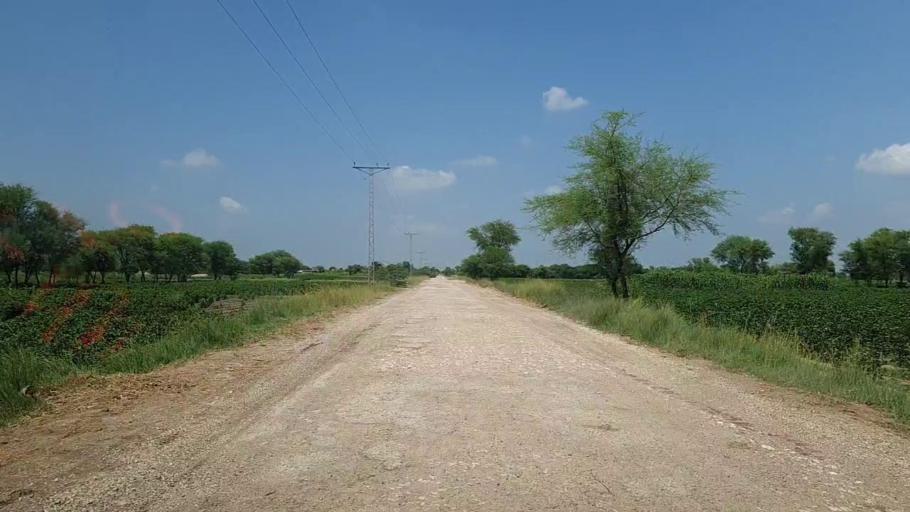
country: PK
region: Sindh
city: Kandiaro
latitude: 26.9939
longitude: 68.2508
